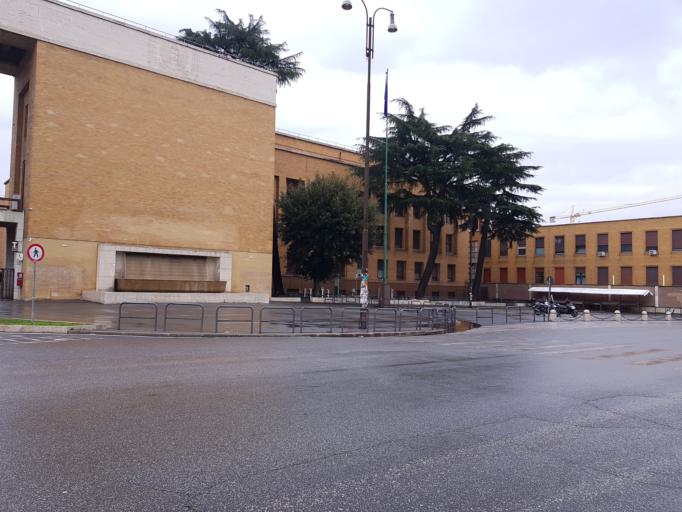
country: IT
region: Latium
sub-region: Citta metropolitana di Roma Capitale
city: Rome
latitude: 41.9020
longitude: 12.5119
